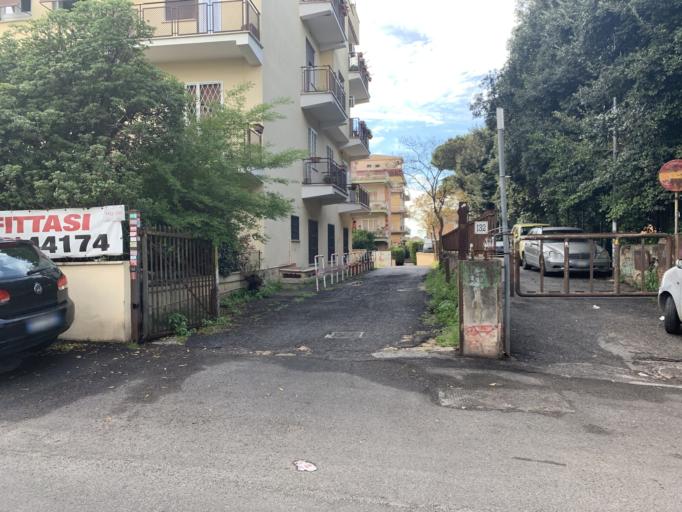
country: VA
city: Vatican City
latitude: 41.8803
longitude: 12.4195
